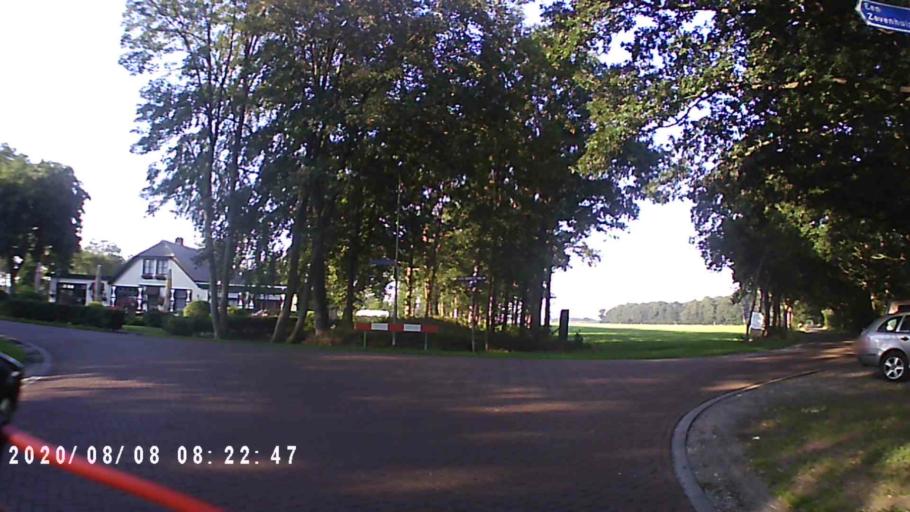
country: NL
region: Groningen
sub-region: Gemeente Leek
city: Leek
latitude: 53.0892
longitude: 6.3113
